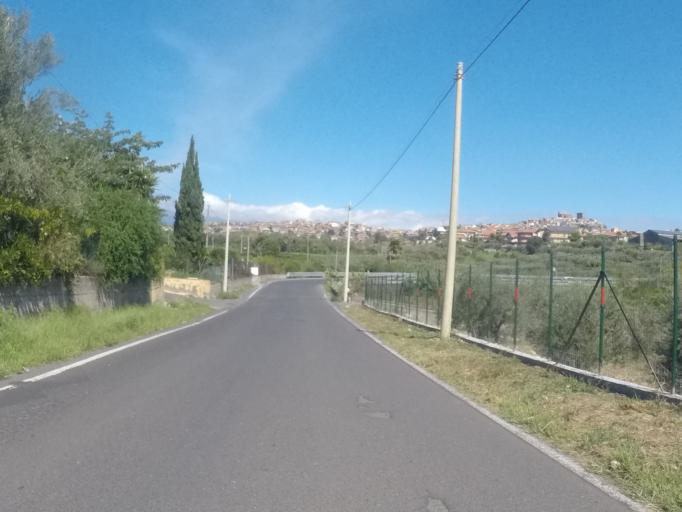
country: IT
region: Sicily
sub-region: Catania
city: Motta Sant'Anastasia
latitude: 37.5031
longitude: 14.9593
